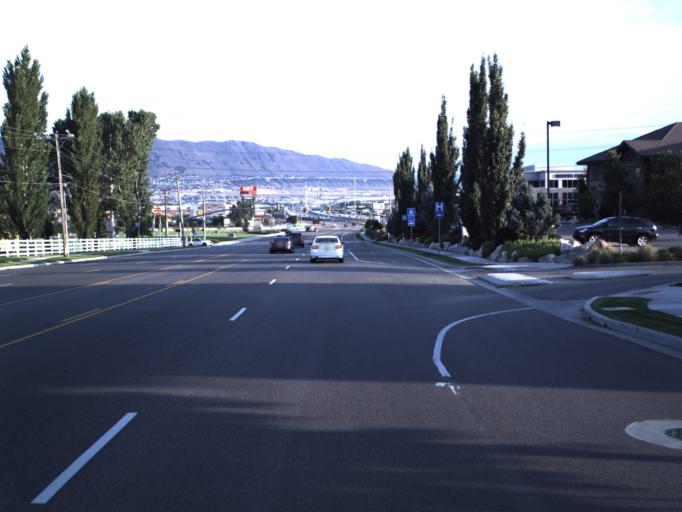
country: US
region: Utah
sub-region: Salt Lake County
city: Draper
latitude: 40.5386
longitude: -111.8915
